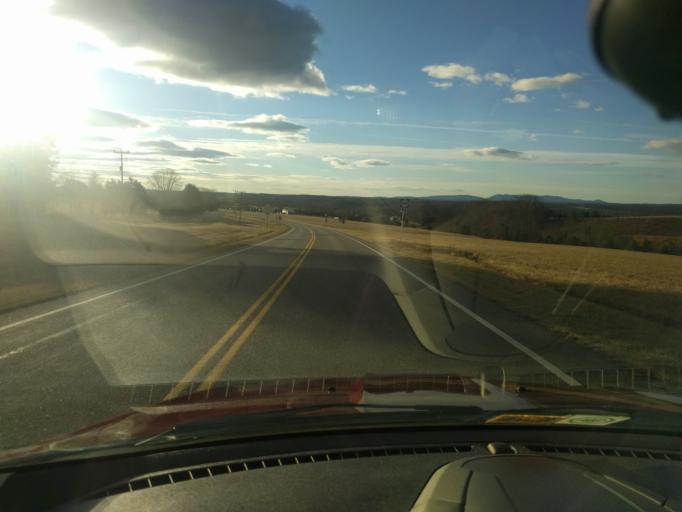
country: US
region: Virginia
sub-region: City of Bedford
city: Bedford
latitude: 37.2612
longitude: -79.5508
